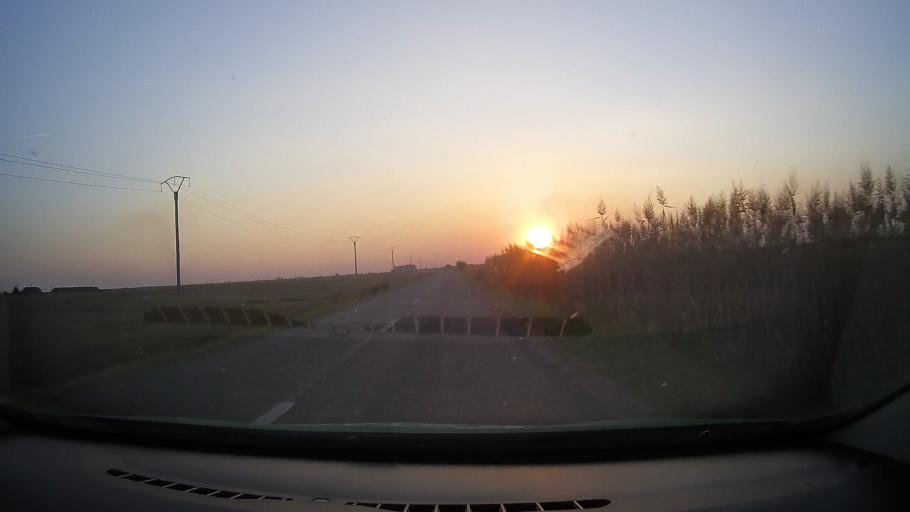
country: RO
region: Arad
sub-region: Comuna Zarand
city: Cintei
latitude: 46.4073
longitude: 21.5897
